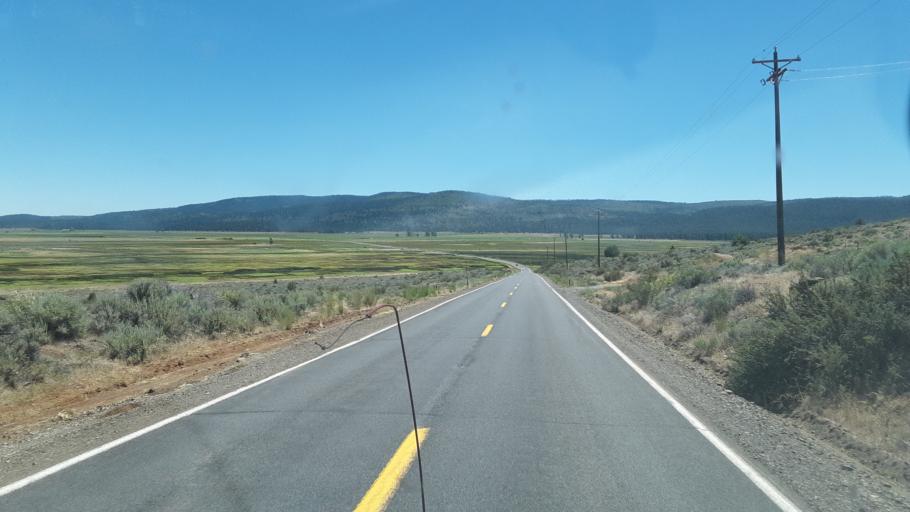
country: US
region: California
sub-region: Lassen County
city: Susanville
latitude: 40.5732
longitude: -120.6421
